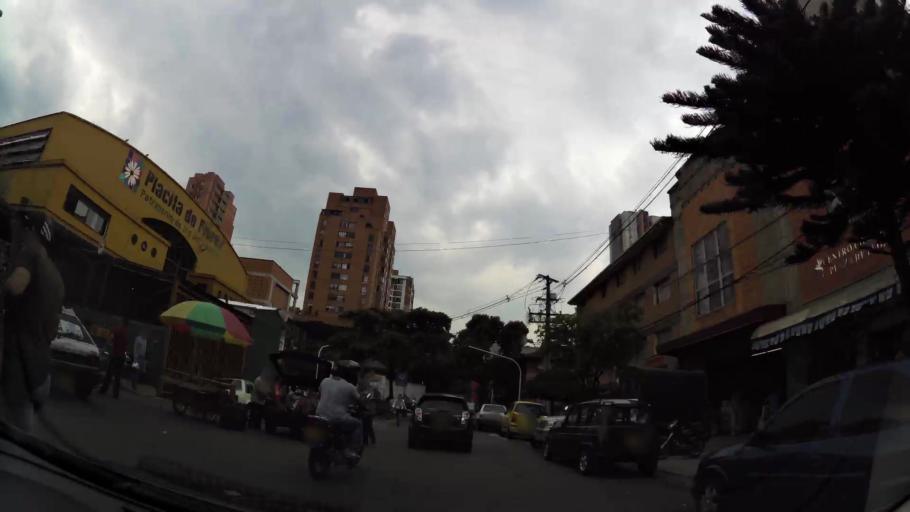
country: CO
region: Antioquia
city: Medellin
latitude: 6.2463
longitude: -75.5603
